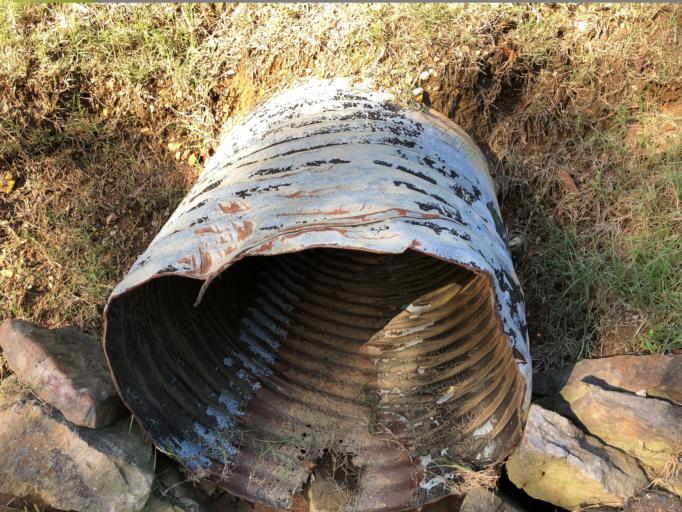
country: US
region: Mississippi
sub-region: De Soto County
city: Horn Lake
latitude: 34.9182
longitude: -89.9690
